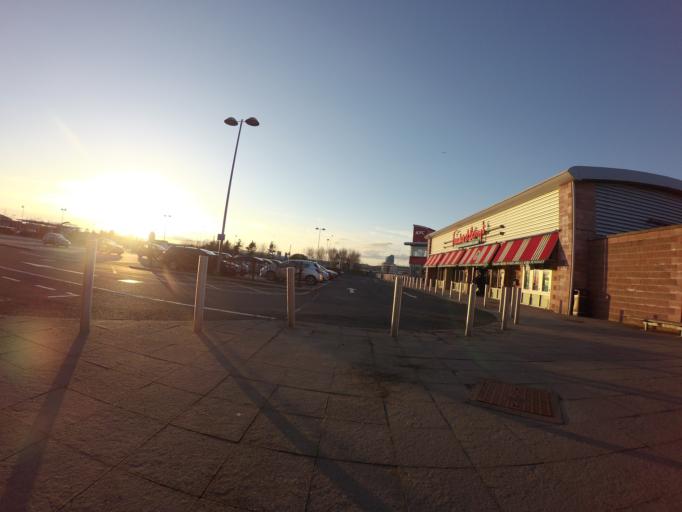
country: GB
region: Scotland
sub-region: West Lothian
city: Livingston
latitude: 55.8793
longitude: -3.5204
